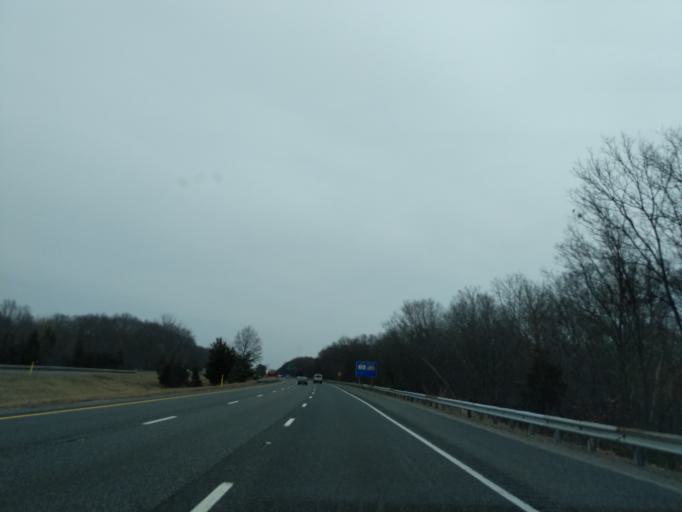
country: US
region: Rhode Island
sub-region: Providence County
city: Valley Falls
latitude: 41.9507
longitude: -71.3705
